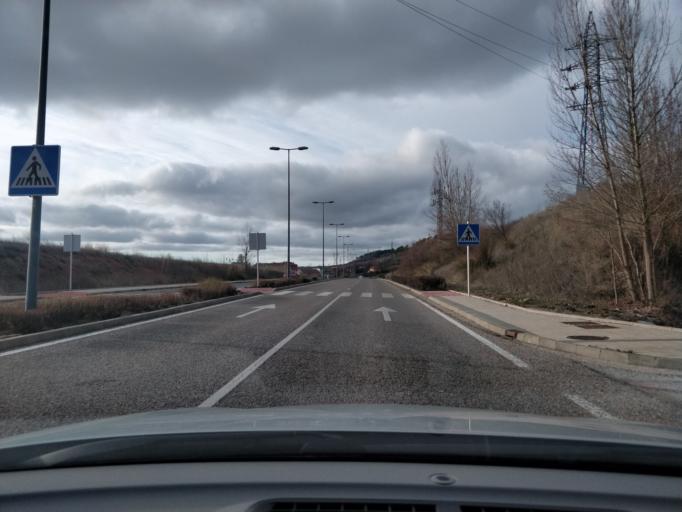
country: ES
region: Castille and Leon
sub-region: Provincia de Burgos
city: Villagonzalo-Pedernales
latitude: 42.3482
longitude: -3.7261
